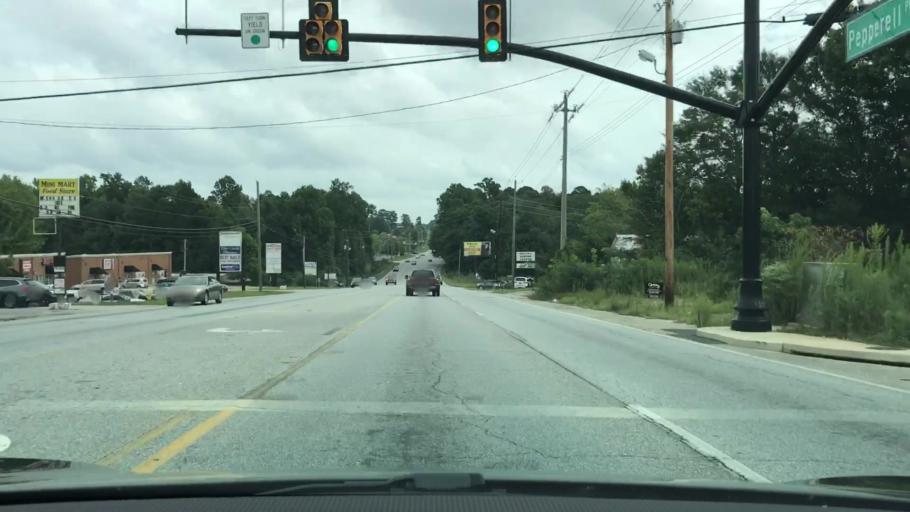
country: US
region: Alabama
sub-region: Lee County
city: Opelika
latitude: 32.6340
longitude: -85.4283
